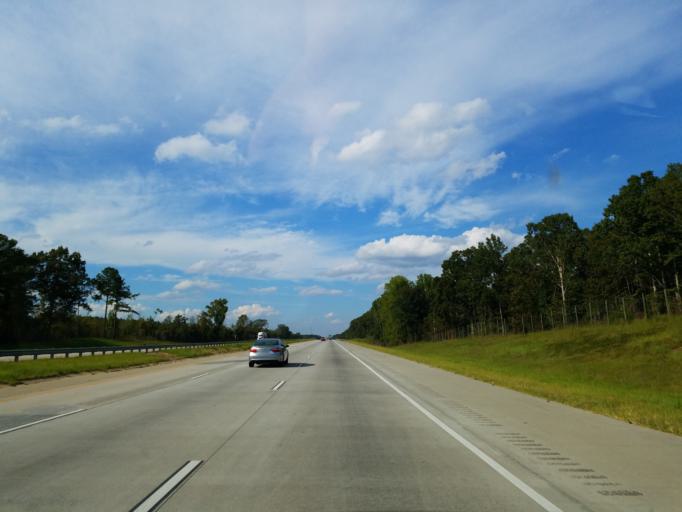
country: US
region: Georgia
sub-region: Dooly County
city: Unadilla
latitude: 32.3074
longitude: -83.7625
